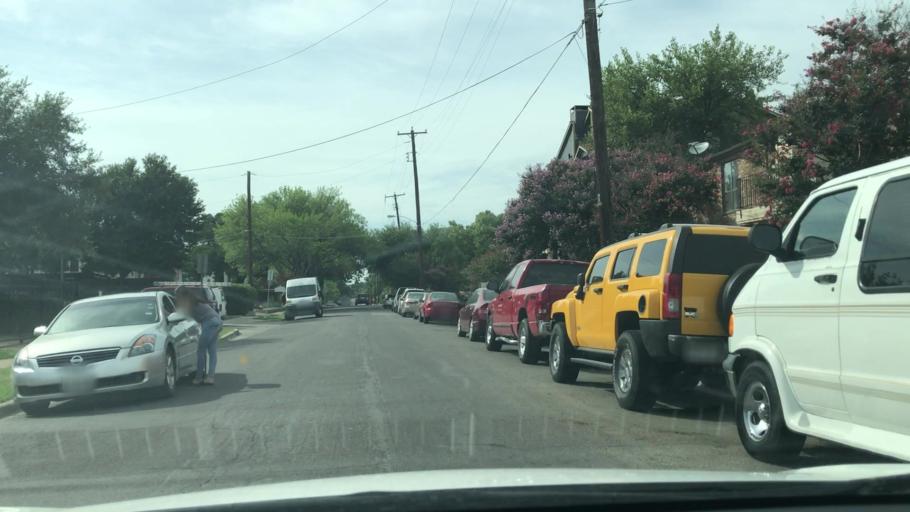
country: US
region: Texas
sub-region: Dallas County
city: Highland Park
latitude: 32.8088
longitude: -96.7753
